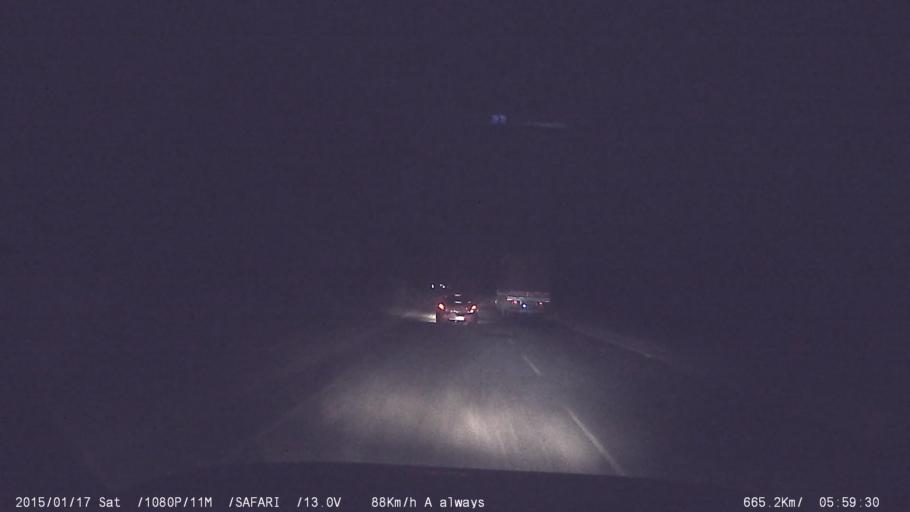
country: IN
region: Tamil Nadu
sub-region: Kancheepuram
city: Kanchipuram
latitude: 12.8978
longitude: 79.5663
